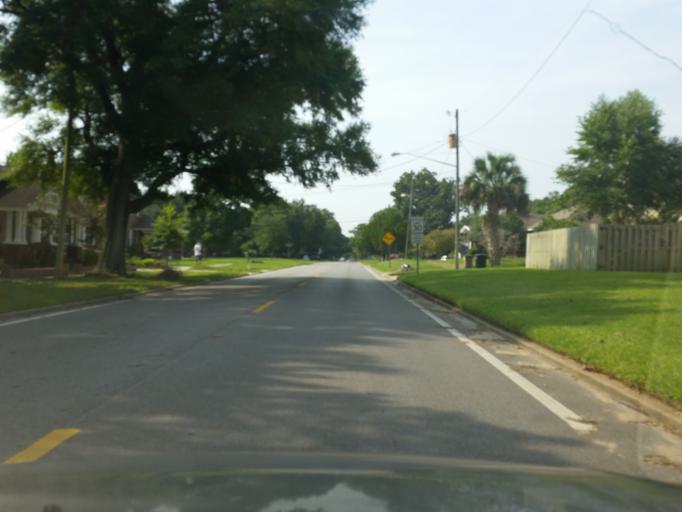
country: US
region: Florida
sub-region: Escambia County
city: East Pensacola Heights
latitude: 30.4298
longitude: -87.1963
